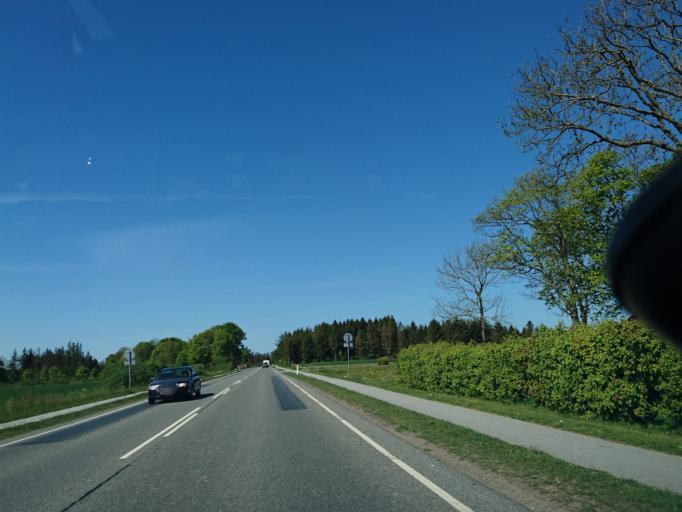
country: DK
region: North Denmark
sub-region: Hjorring Kommune
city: Tars
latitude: 57.4552
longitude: 10.1204
